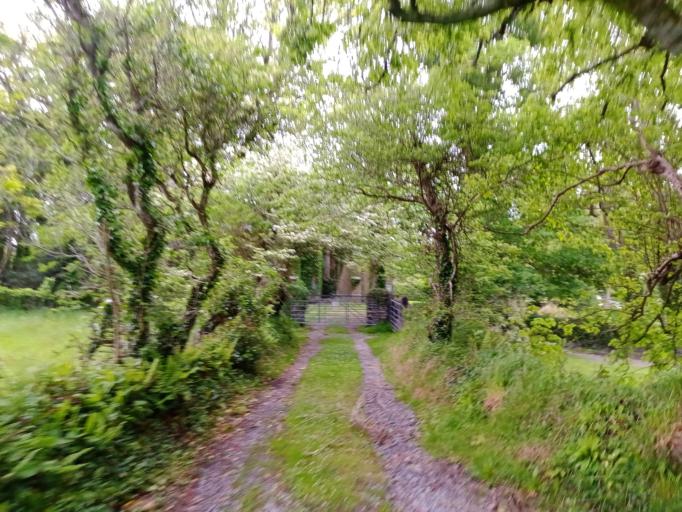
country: IE
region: Munster
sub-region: County Cork
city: Skibbereen
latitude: 51.5222
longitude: -9.3366
